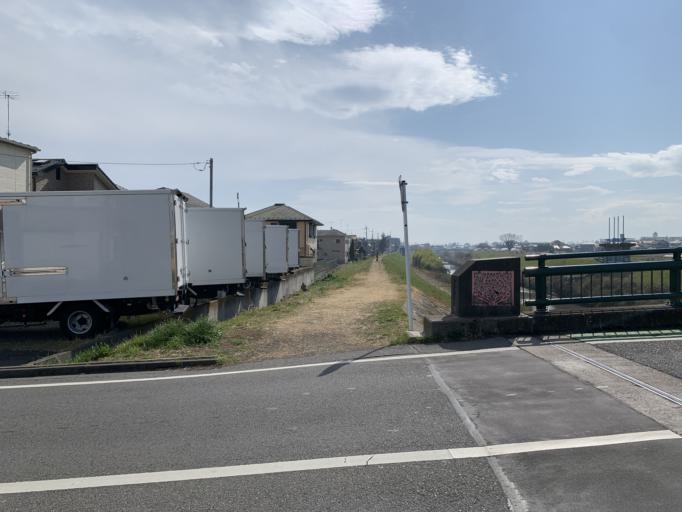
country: JP
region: Saitama
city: Yono
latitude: 35.8777
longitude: 139.6022
